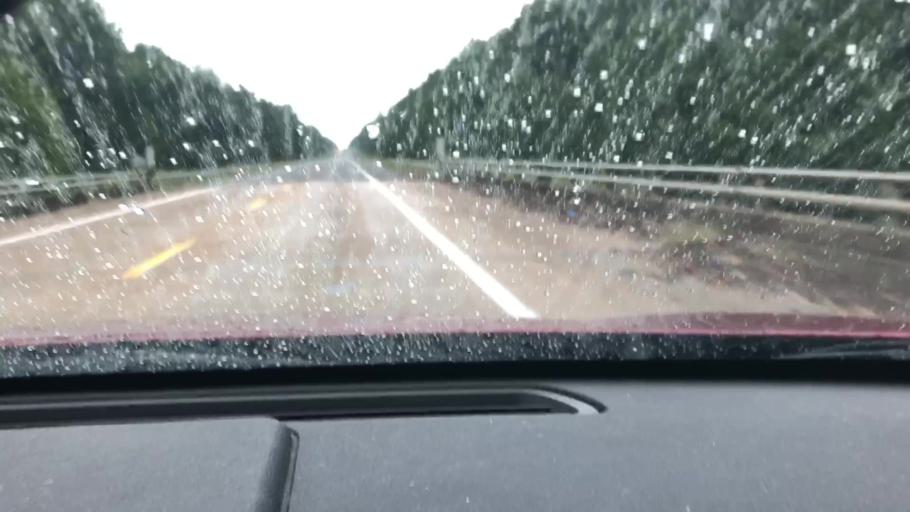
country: US
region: Arkansas
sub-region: Columbia County
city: Magnolia
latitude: 33.3034
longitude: -93.2705
